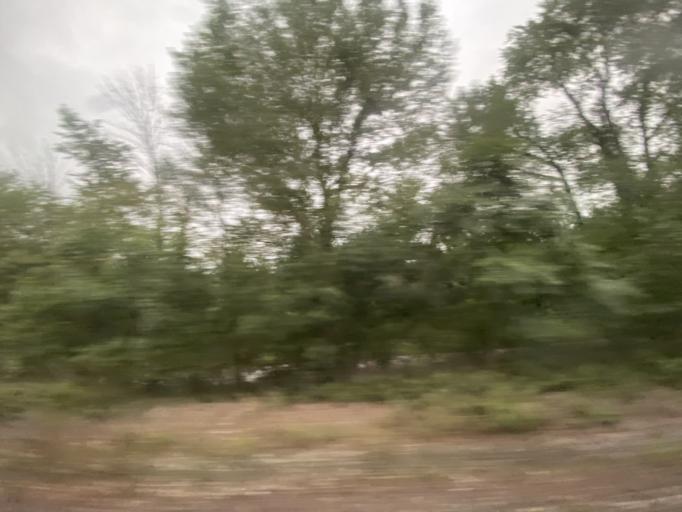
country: US
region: Indiana
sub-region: LaPorte County
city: Westville
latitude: 41.5984
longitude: -86.9173
